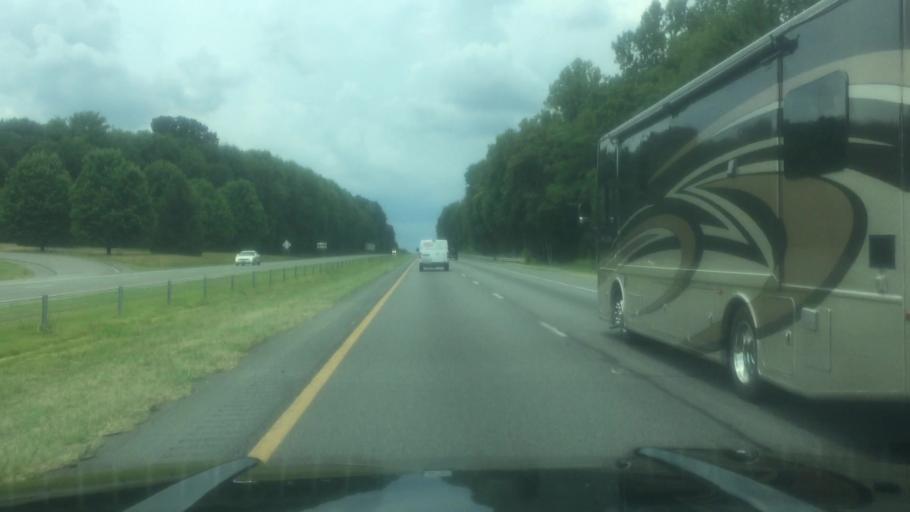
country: US
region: North Carolina
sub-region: Surry County
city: Pilot Mountain
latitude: 36.3431
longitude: -80.4604
